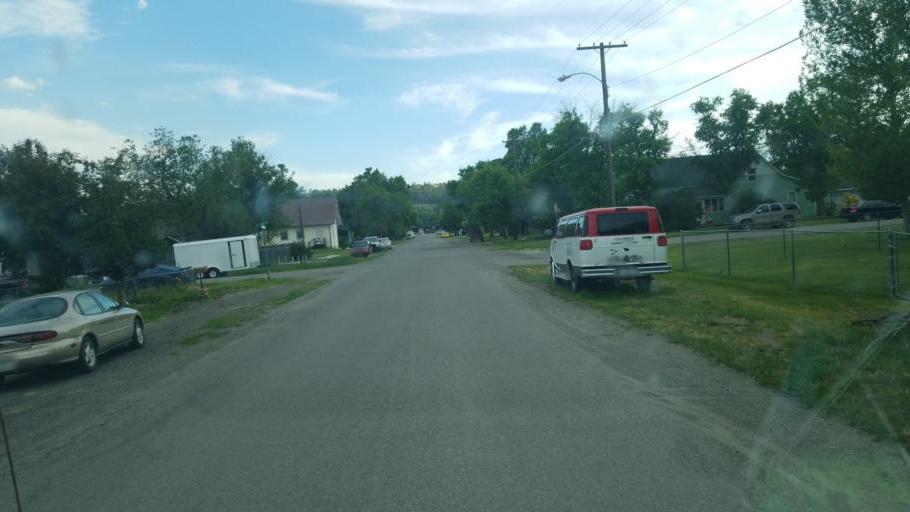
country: US
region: Montana
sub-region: Stillwater County
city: Columbus
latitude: 45.6399
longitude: -109.2495
